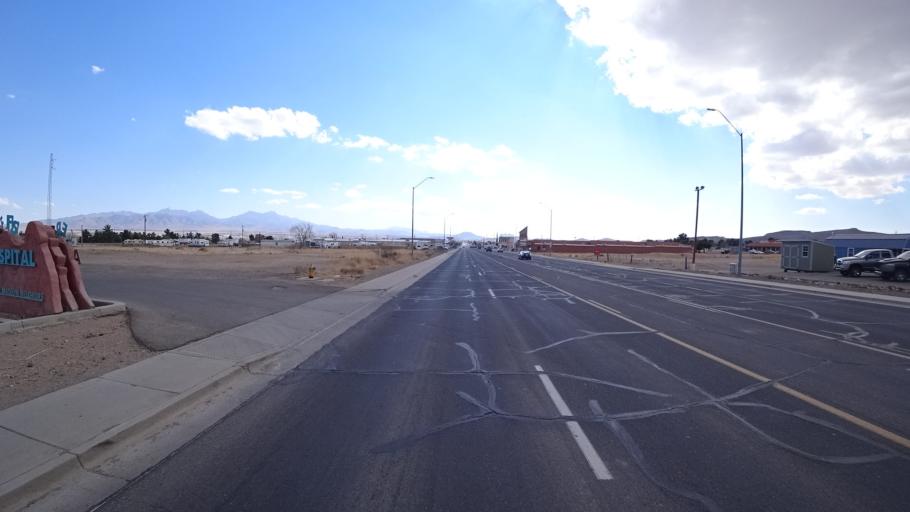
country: US
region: Arizona
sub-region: Mohave County
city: New Kingman-Butler
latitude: 35.2427
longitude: -114.0380
